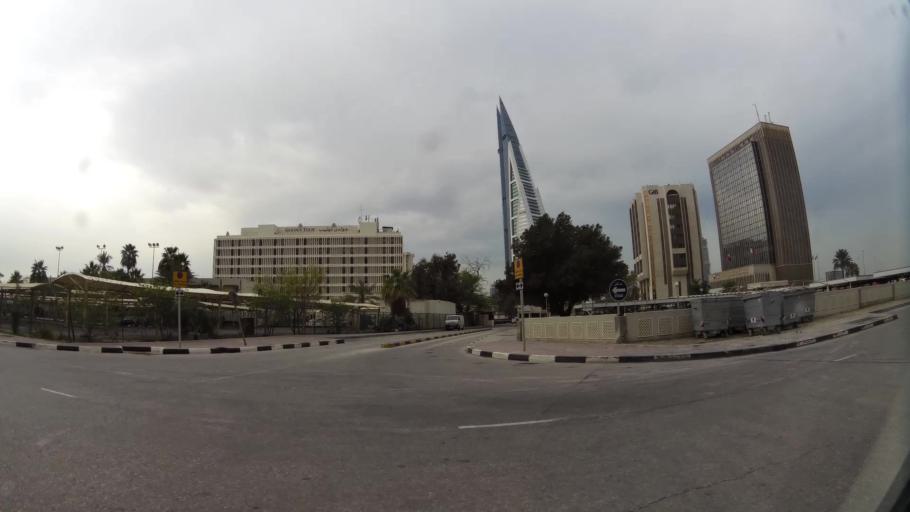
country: BH
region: Manama
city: Manama
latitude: 26.2413
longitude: 50.5858
